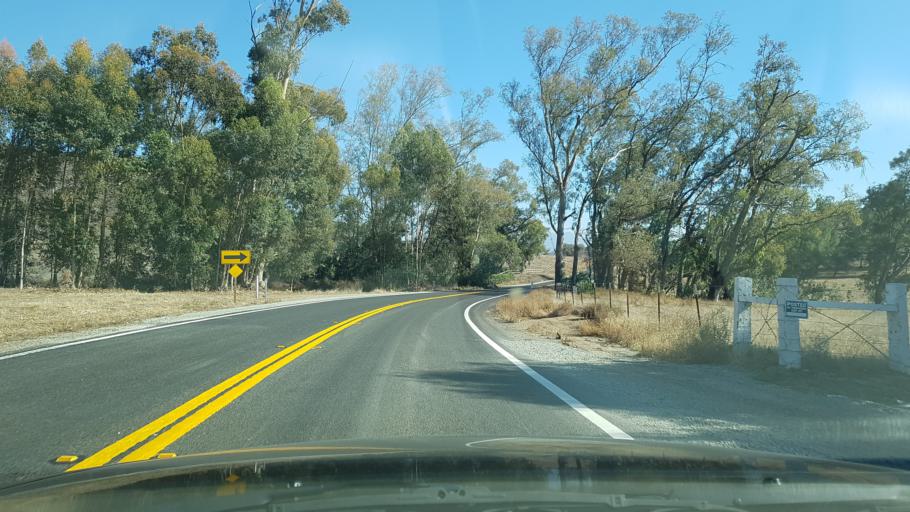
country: US
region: California
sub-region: San Diego County
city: San Diego Country Estates
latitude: 33.0752
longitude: -116.7716
